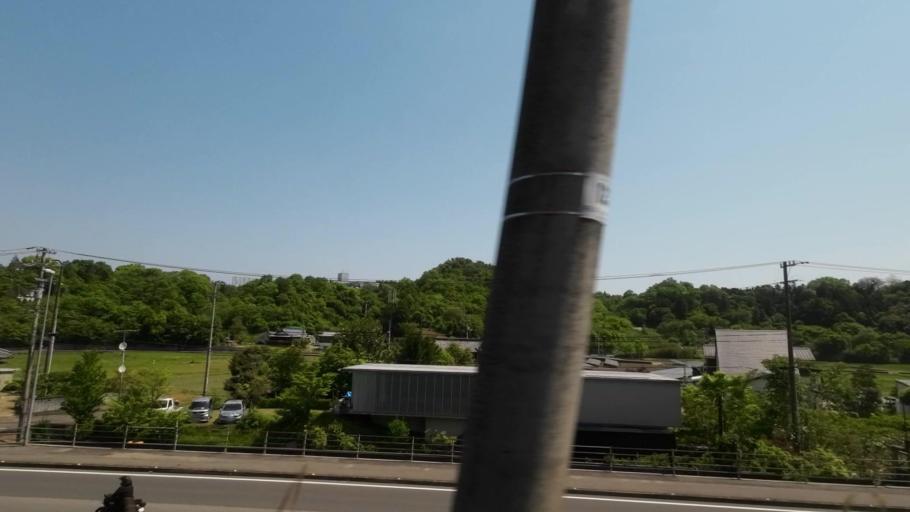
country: JP
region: Ehime
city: Saijo
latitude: 33.9914
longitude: 133.0510
